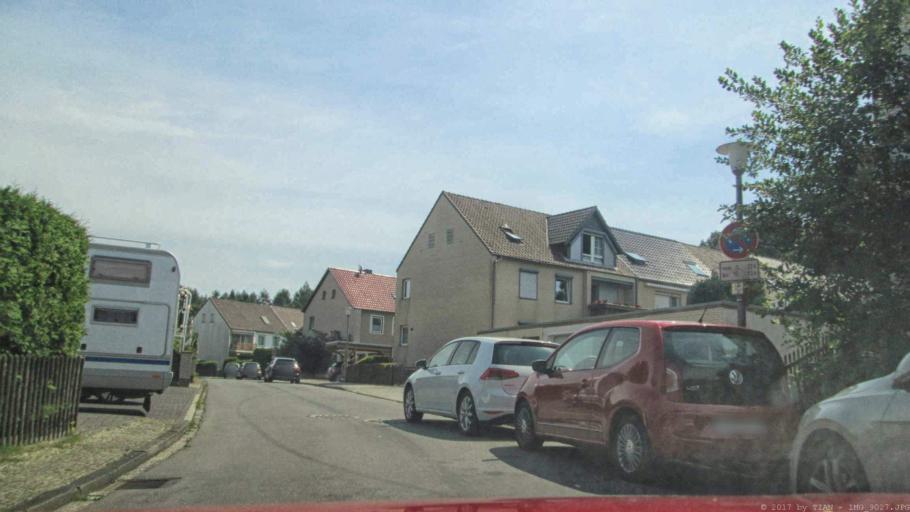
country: DE
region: Lower Saxony
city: Wolfsburg
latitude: 52.4187
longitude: 10.8108
